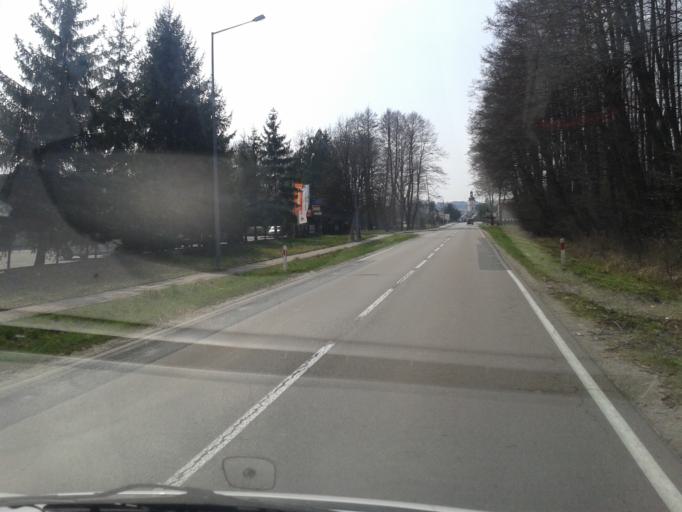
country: PL
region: Subcarpathian Voivodeship
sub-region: Powiat lubaczowski
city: Narol
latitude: 50.3553
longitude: 23.3292
